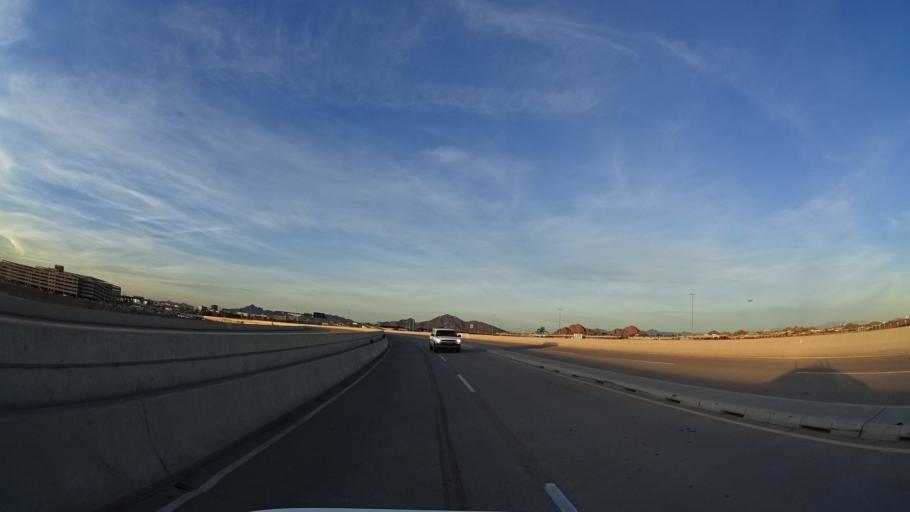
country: US
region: Arizona
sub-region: Maricopa County
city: Tempe Junction
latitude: 33.4312
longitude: -111.9794
